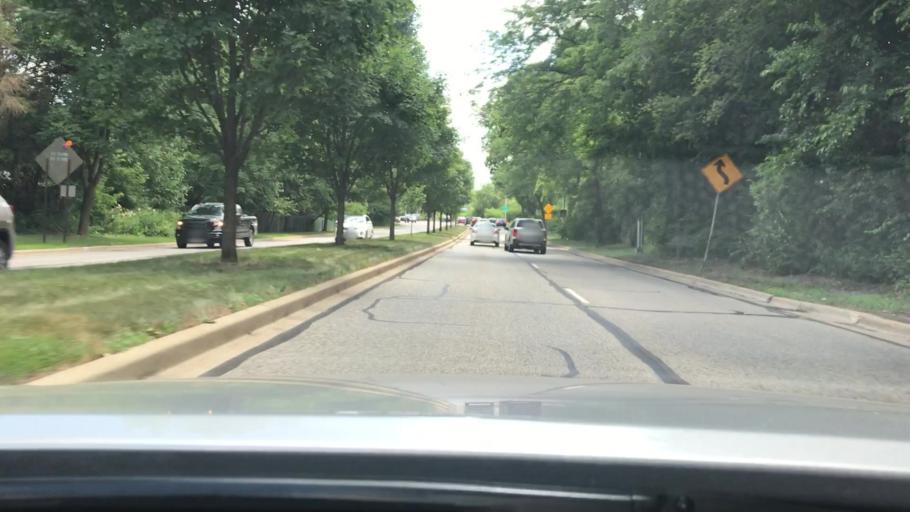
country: US
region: Illinois
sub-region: DuPage County
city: Naperville
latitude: 41.7942
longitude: -88.1189
